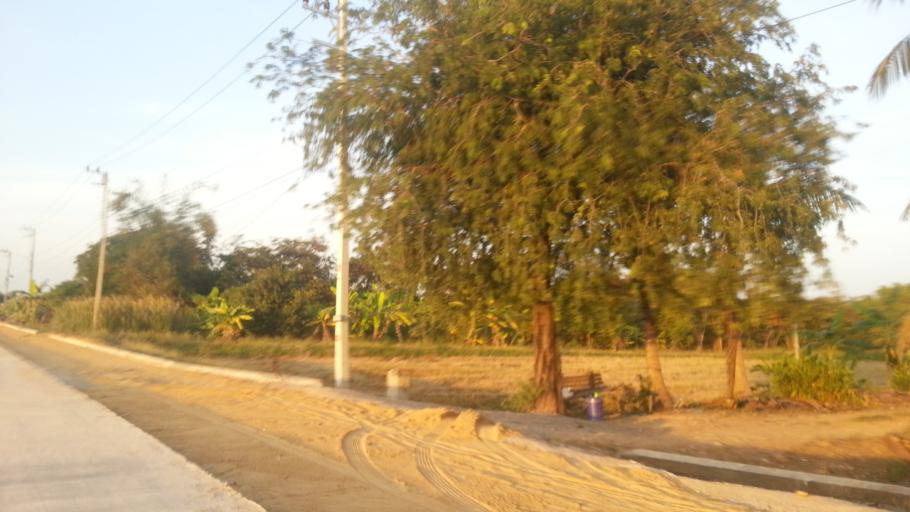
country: TH
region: Pathum Thani
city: Nong Suea
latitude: 14.0407
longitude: 100.8666
